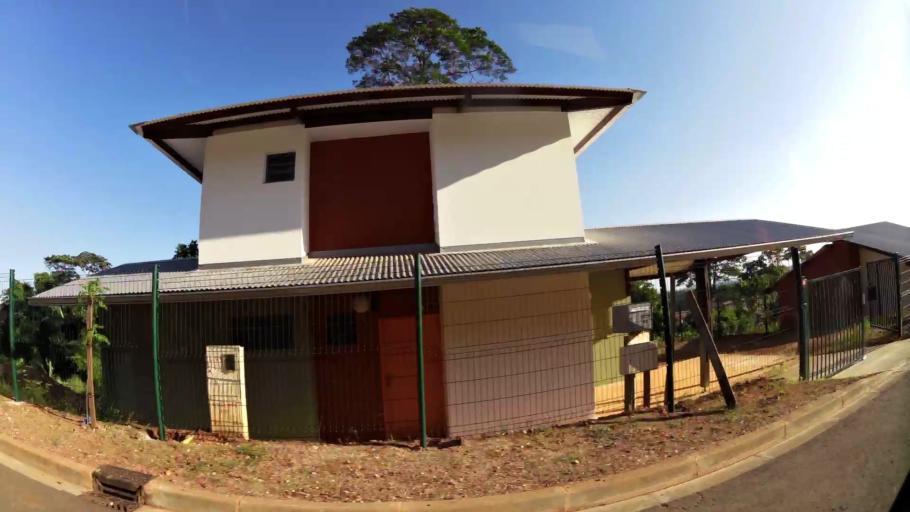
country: GF
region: Guyane
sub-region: Guyane
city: Remire-Montjoly
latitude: 4.8880
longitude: -52.2964
